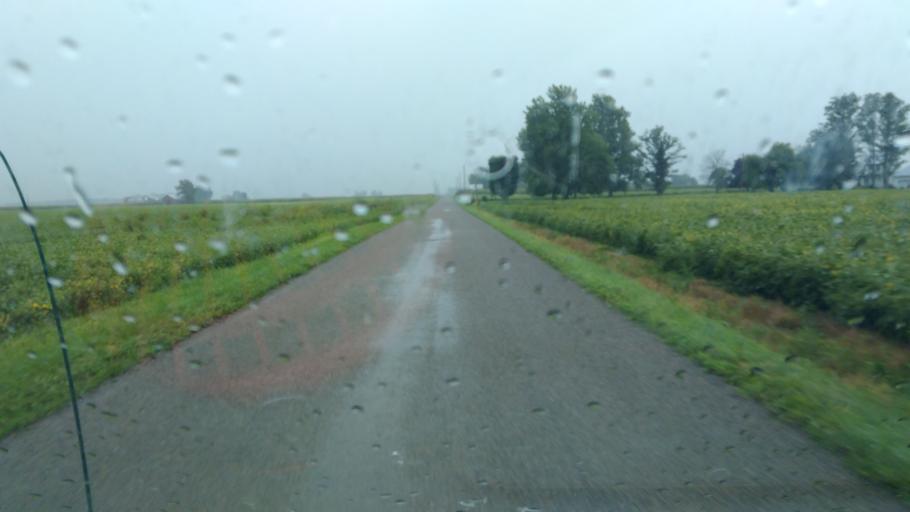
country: US
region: Ohio
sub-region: Hardin County
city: Kenton
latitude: 40.7142
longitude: -83.5951
